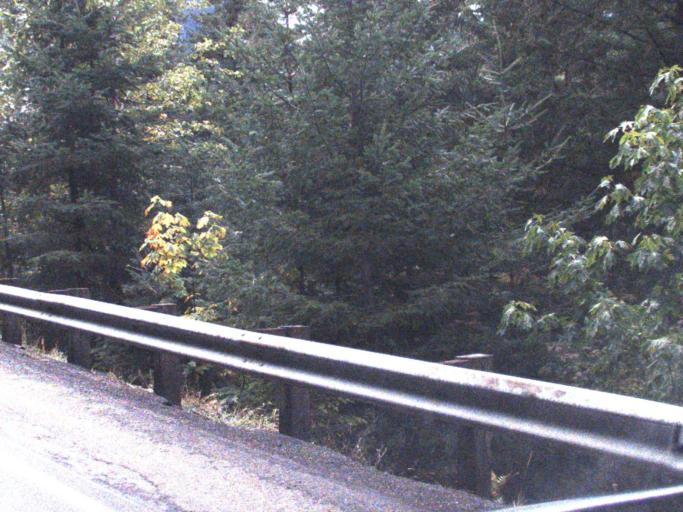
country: US
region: Washington
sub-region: Pierce County
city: Buckley
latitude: 46.6805
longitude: -121.5410
